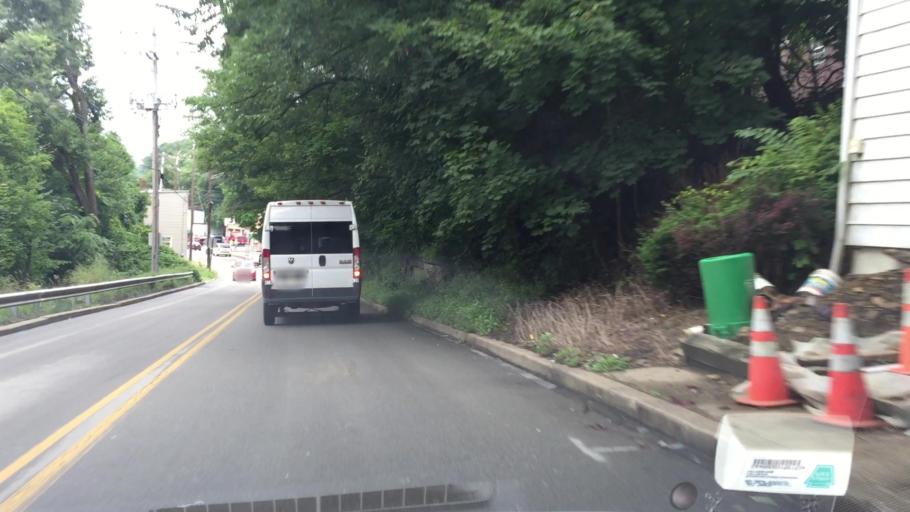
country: US
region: Pennsylvania
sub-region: Allegheny County
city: Millvale
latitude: 40.4836
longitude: -79.9718
